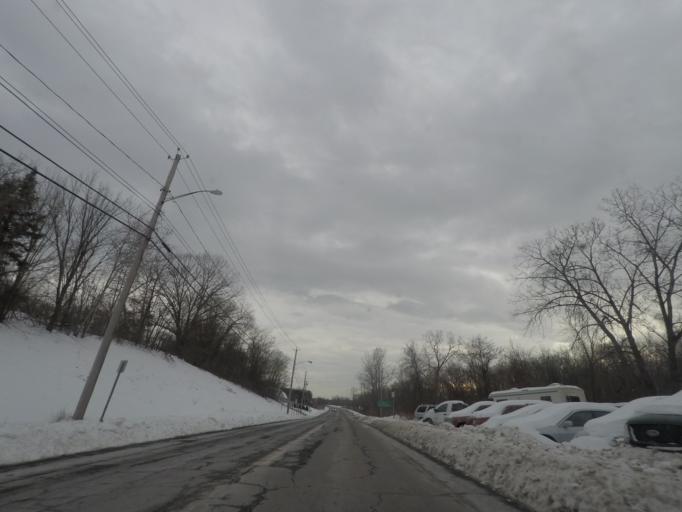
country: US
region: New York
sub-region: Rensselaer County
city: Hampton Manor
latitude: 42.6189
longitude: -73.7460
